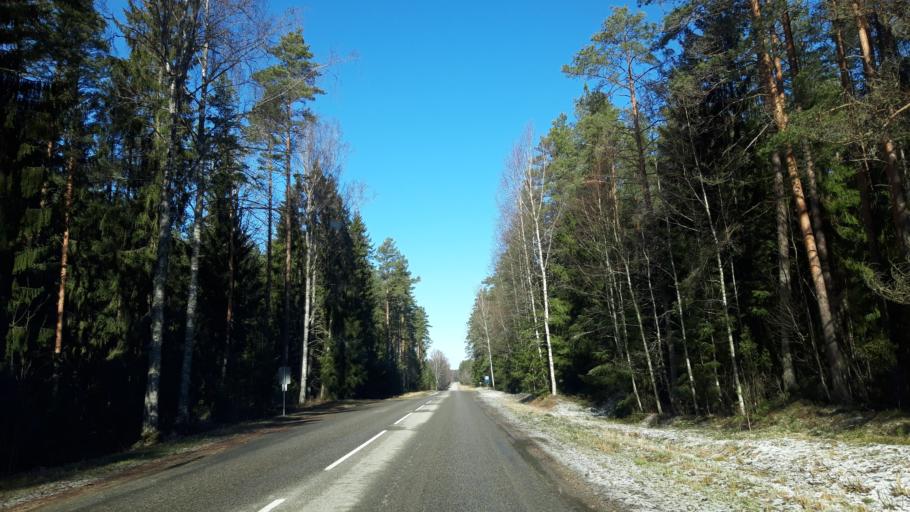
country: LV
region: Strenci
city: Strenci
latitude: 57.6008
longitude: 25.7163
